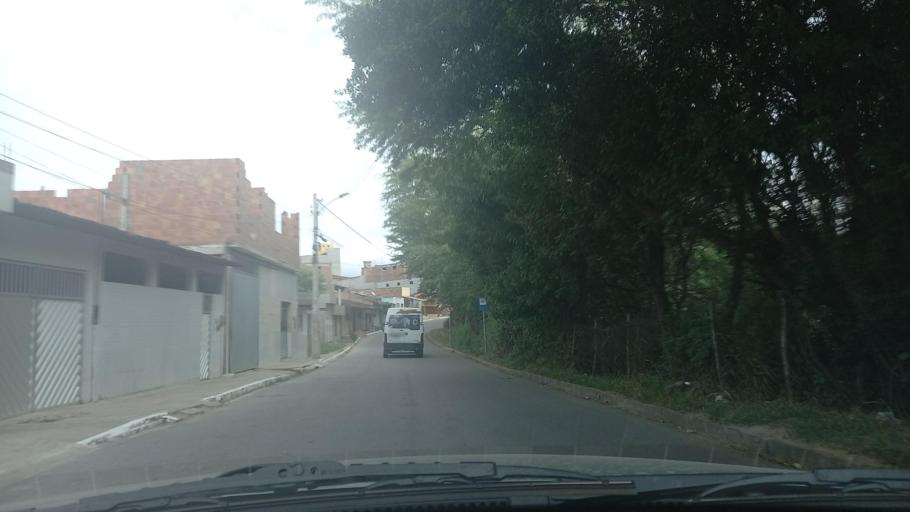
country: BR
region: Pernambuco
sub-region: Caruaru
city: Caruaru
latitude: -8.2901
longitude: -36.0304
